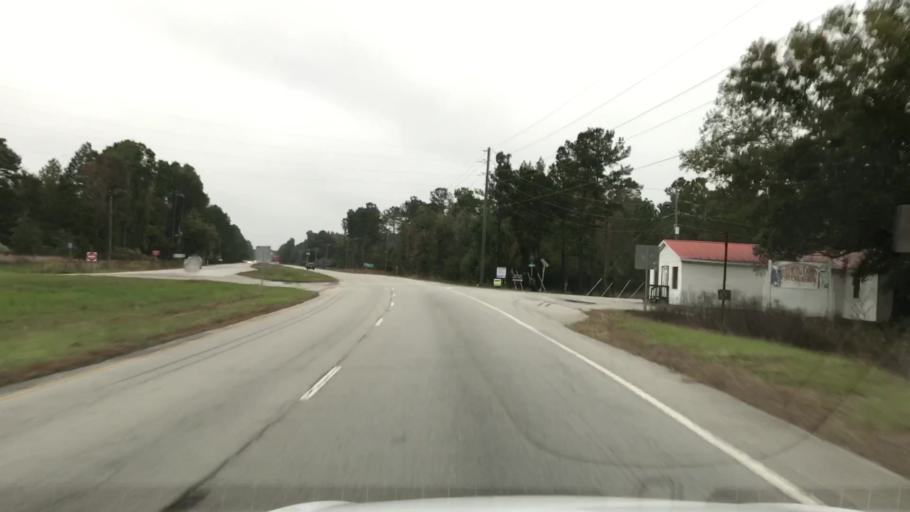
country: US
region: South Carolina
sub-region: Charleston County
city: Awendaw
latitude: 32.9900
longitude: -79.6461
